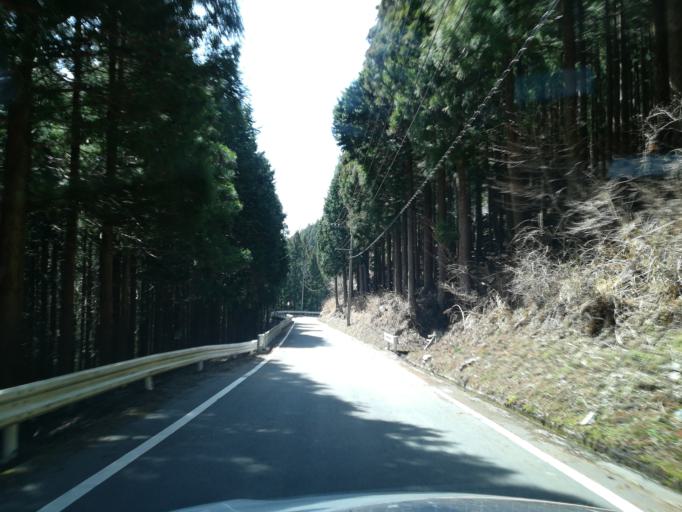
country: JP
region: Tokushima
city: Wakimachi
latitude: 33.8615
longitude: 134.0643
